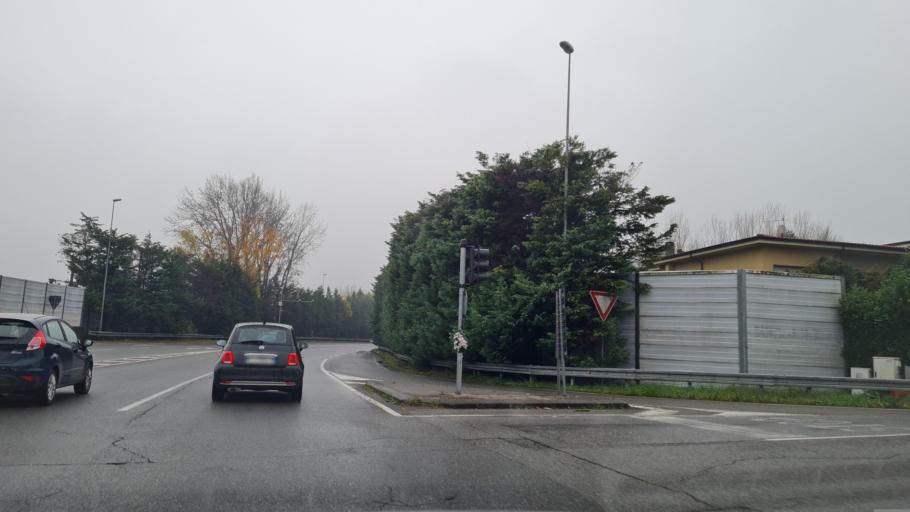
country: IT
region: Tuscany
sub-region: Provincia di Lucca
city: Lucca
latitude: 43.8367
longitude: 10.4764
